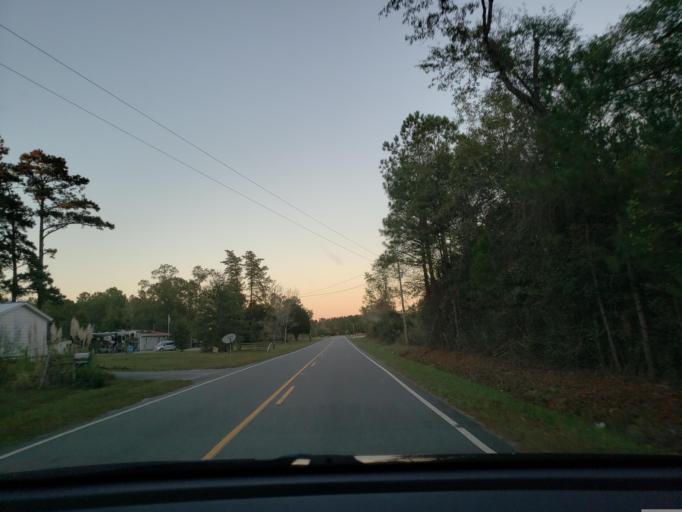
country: US
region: North Carolina
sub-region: Onslow County
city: Richlands
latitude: 34.7301
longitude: -77.6249
